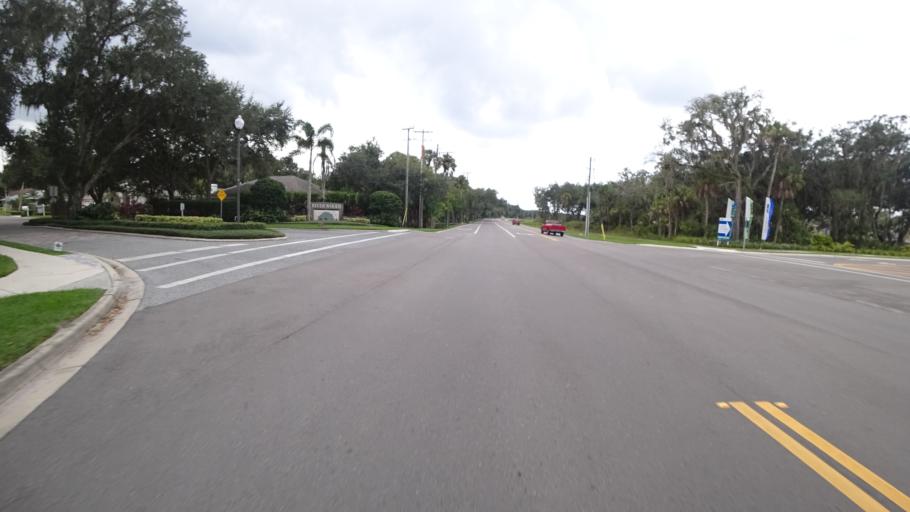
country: US
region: Florida
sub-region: Manatee County
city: Ellenton
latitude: 27.5449
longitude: -82.4517
